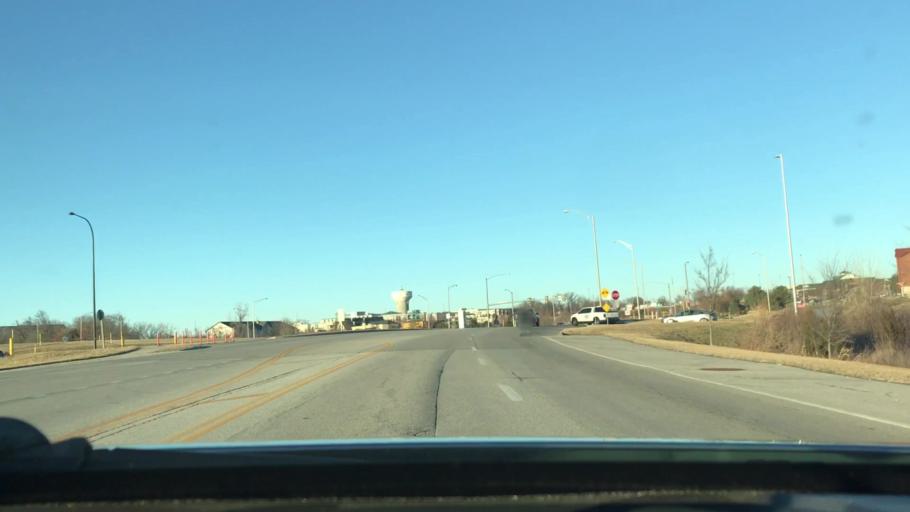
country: US
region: Kansas
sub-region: Wyandotte County
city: Edwardsville
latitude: 39.1150
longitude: -94.8200
